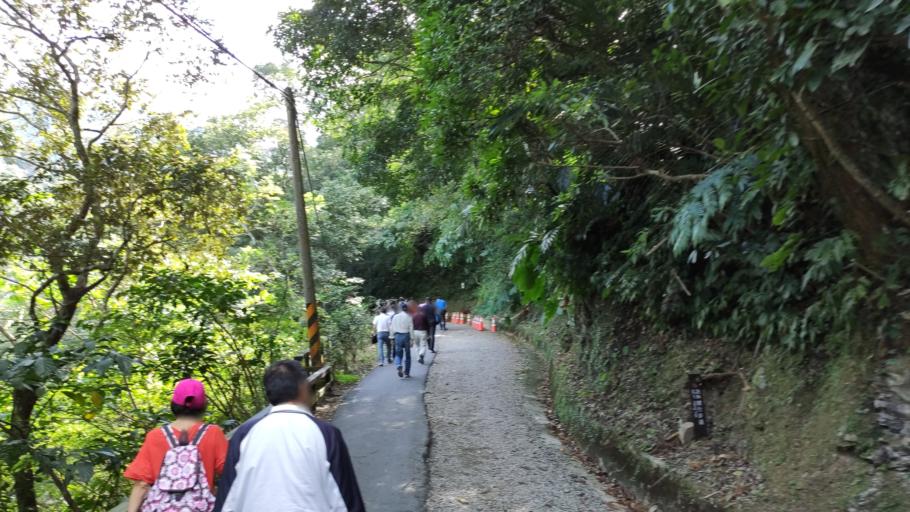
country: TW
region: Taiwan
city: Daxi
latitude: 24.8290
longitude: 121.4448
